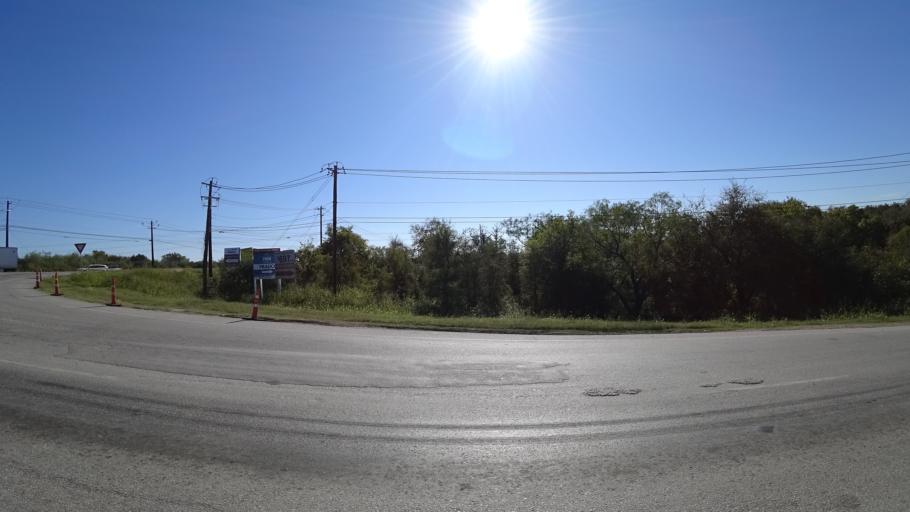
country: US
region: Texas
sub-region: Travis County
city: Hornsby Bend
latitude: 30.2565
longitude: -97.6122
